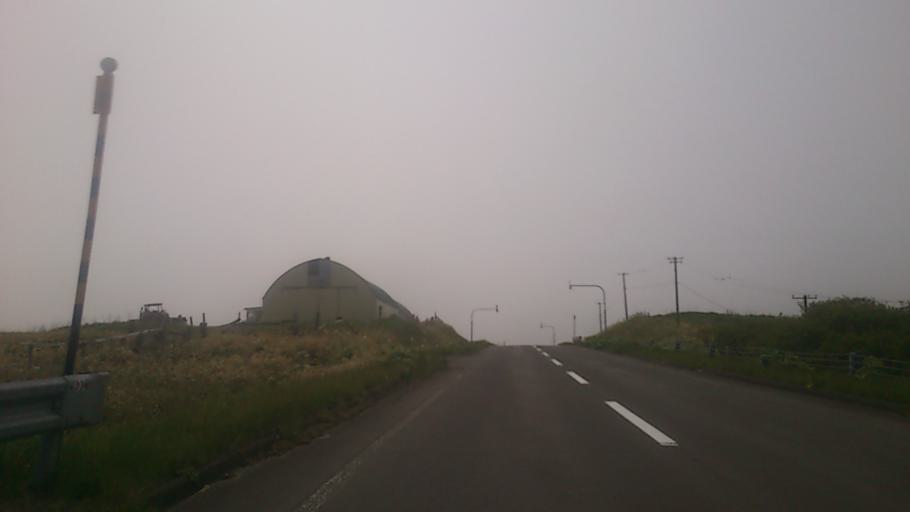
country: JP
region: Hokkaido
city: Nemuro
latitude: 43.1759
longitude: 145.3048
